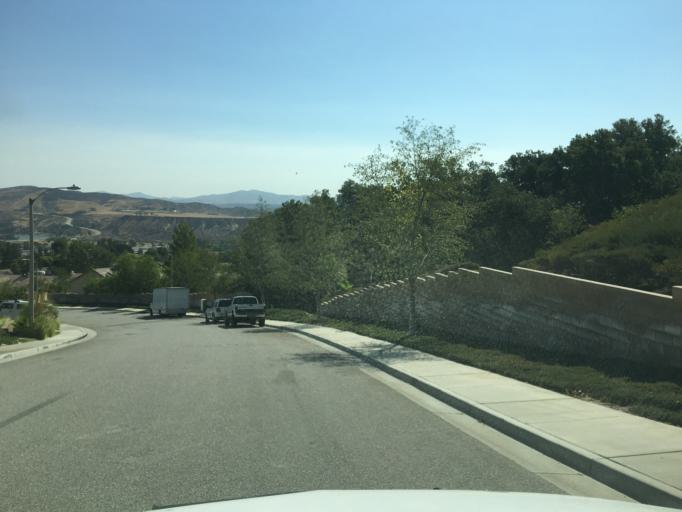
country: US
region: California
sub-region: Los Angeles County
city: Castaic
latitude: 34.4870
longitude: -118.6276
